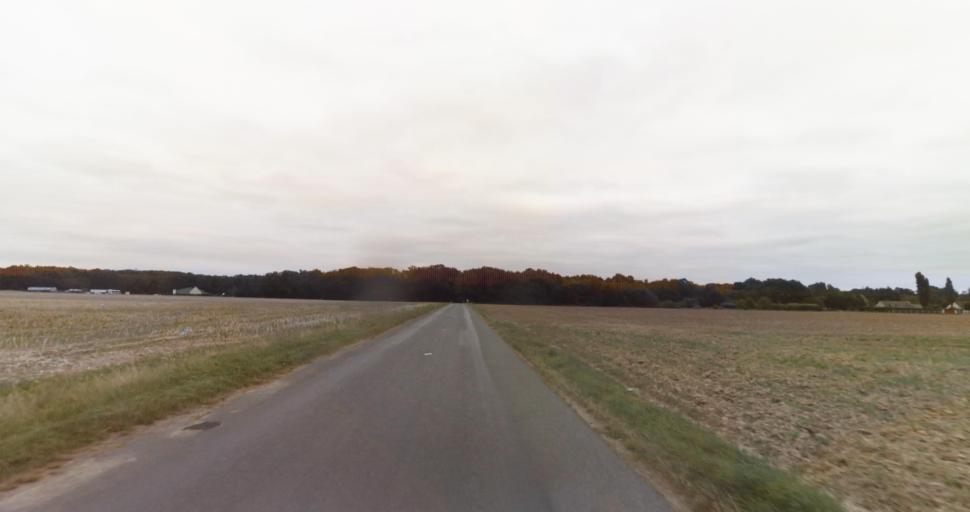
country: FR
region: Haute-Normandie
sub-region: Departement de l'Eure
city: Saint-Germain-sur-Avre
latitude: 48.8035
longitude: 1.2729
